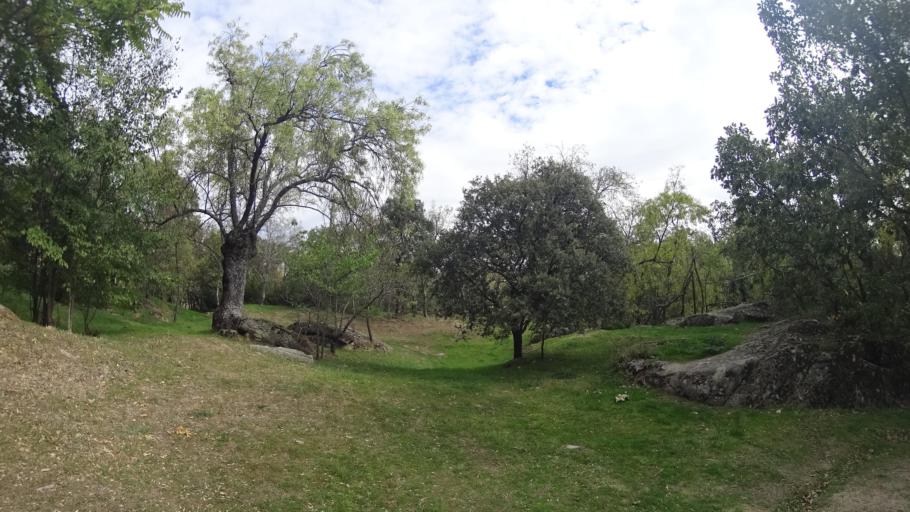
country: ES
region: Madrid
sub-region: Provincia de Madrid
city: El Escorial
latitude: 40.5865
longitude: -4.1361
